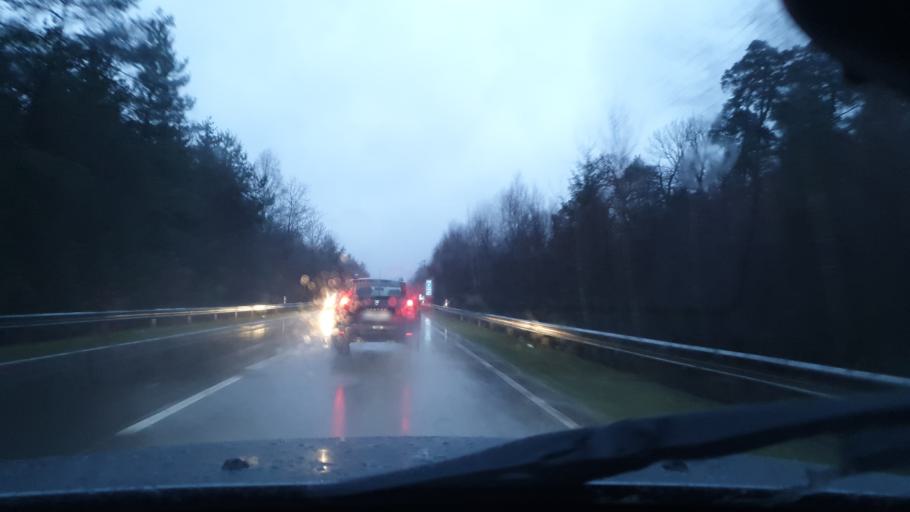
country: DE
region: Rheinland-Pfalz
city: Schonenberg-Kubelberg
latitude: 49.3689
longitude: 7.3715
